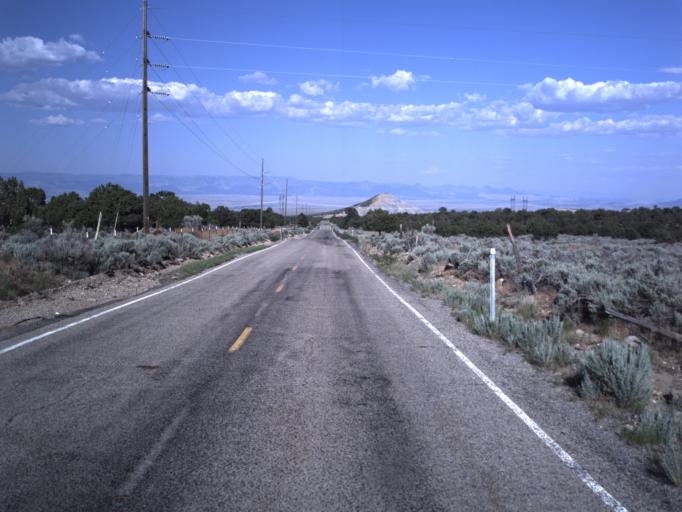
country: US
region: Utah
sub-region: Emery County
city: Huntington
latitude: 39.4842
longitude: -110.9927
